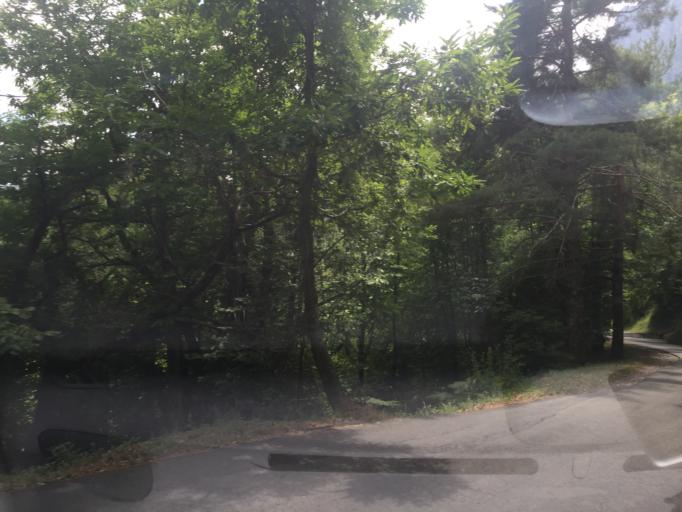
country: IT
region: Tuscany
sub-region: Provincia di Lucca
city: Fontana delle Monache
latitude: 44.1280
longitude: 10.2594
